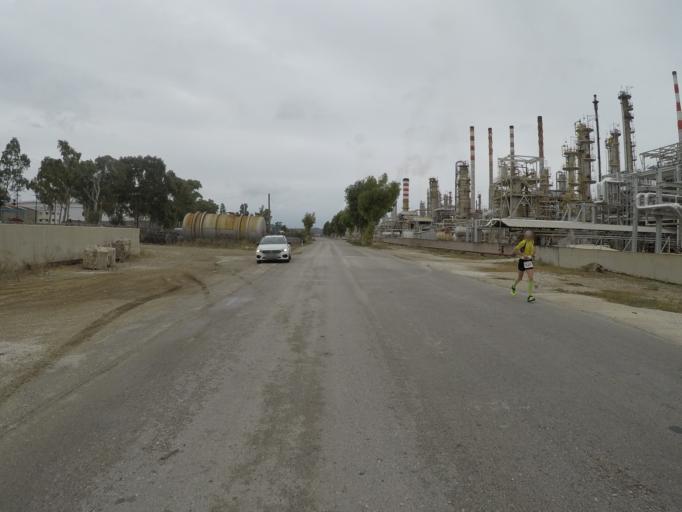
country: GR
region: Peloponnese
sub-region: Nomos Korinthias
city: Isthmia
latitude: 37.9193
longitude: 23.0677
